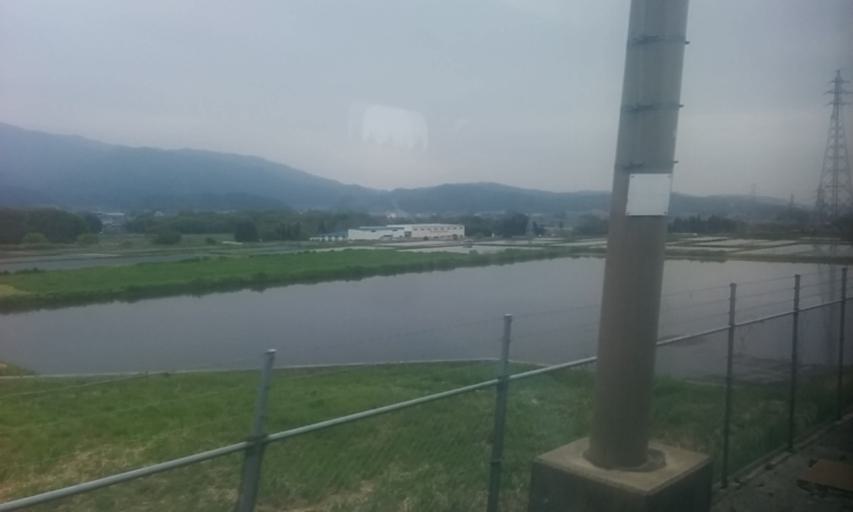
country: JP
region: Gifu
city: Tarui
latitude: 35.3718
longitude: 136.5046
